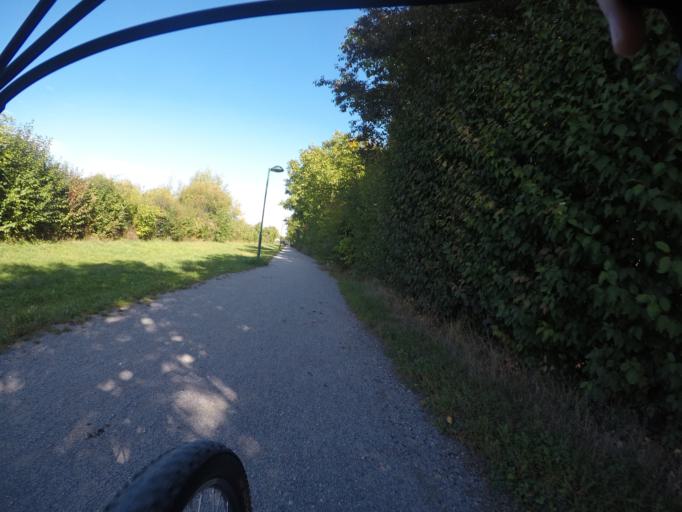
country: AT
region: Lower Austria
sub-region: Politischer Bezirk Modling
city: Brunn am Gebirge
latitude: 48.1057
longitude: 16.2989
